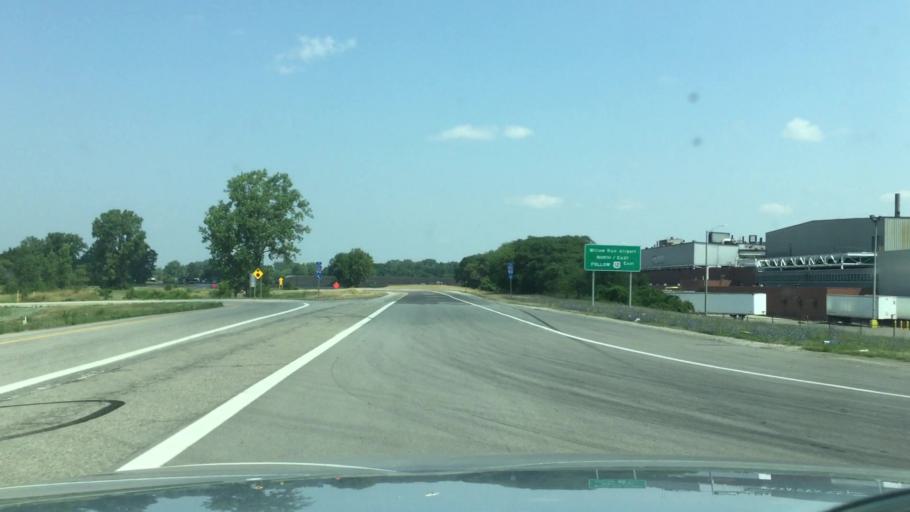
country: US
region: Michigan
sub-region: Washtenaw County
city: Ypsilanti
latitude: 42.2326
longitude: -83.5615
